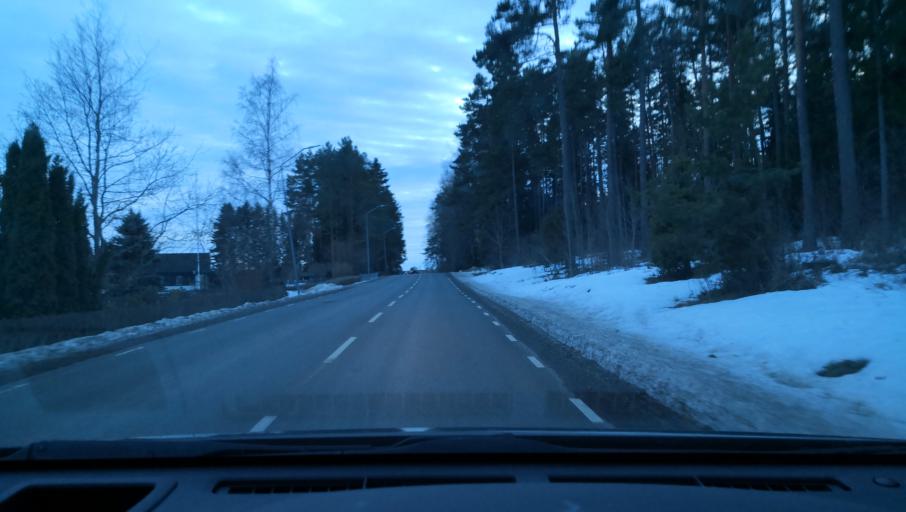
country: SE
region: Uppsala
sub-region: Osthammars Kommun
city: Bjorklinge
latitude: 60.0949
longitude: 17.5599
